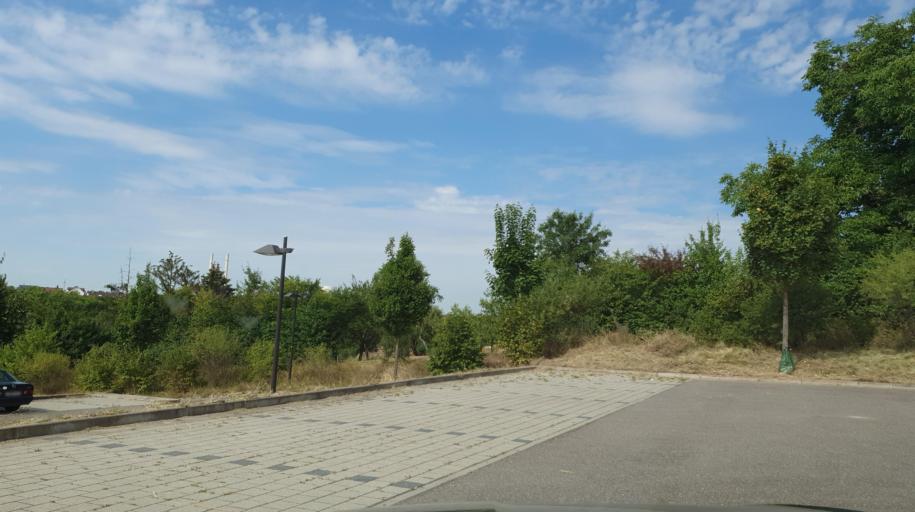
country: DE
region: Baden-Wuerttemberg
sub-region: Regierungsbezirk Stuttgart
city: Neckarsulm
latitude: 49.1904
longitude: 9.2423
